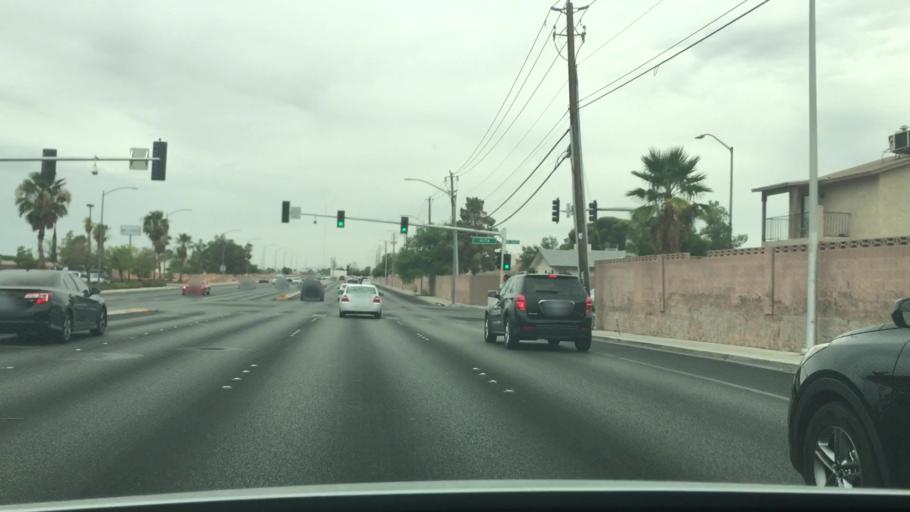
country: US
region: Nevada
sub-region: Clark County
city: Spring Valley
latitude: 36.1669
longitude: -115.2600
